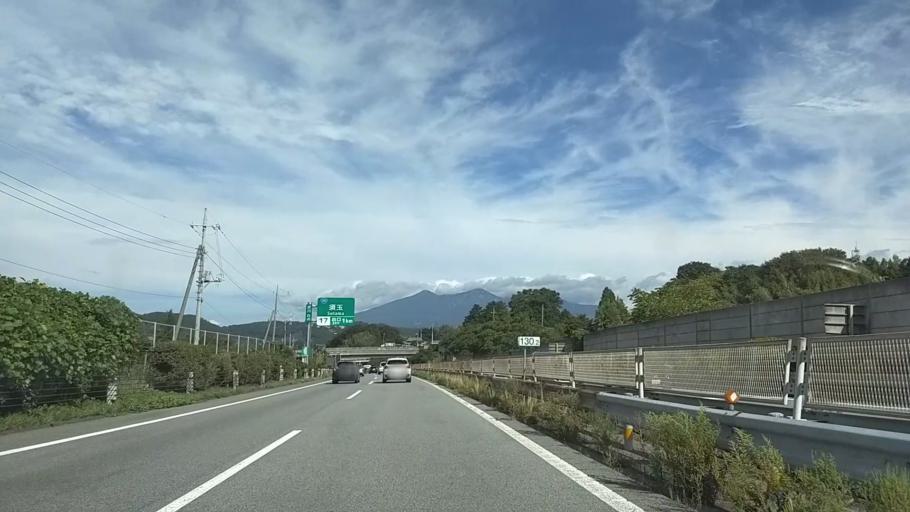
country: JP
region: Yamanashi
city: Nirasaki
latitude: 35.7641
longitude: 138.4322
